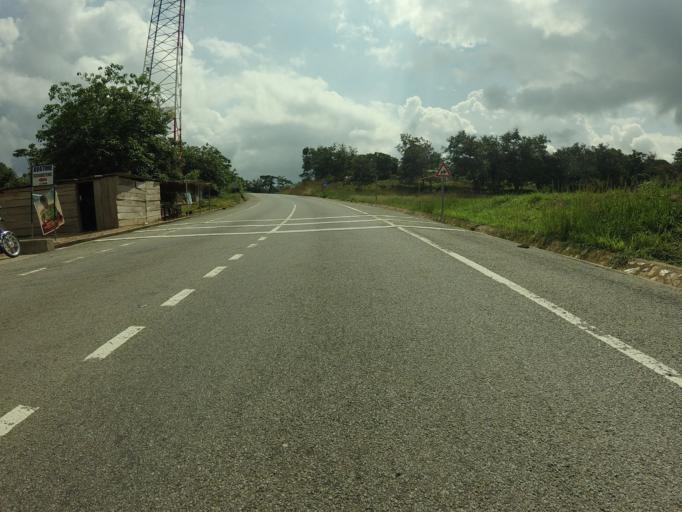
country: GH
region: Volta
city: Kpandu
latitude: 6.8243
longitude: 0.4206
